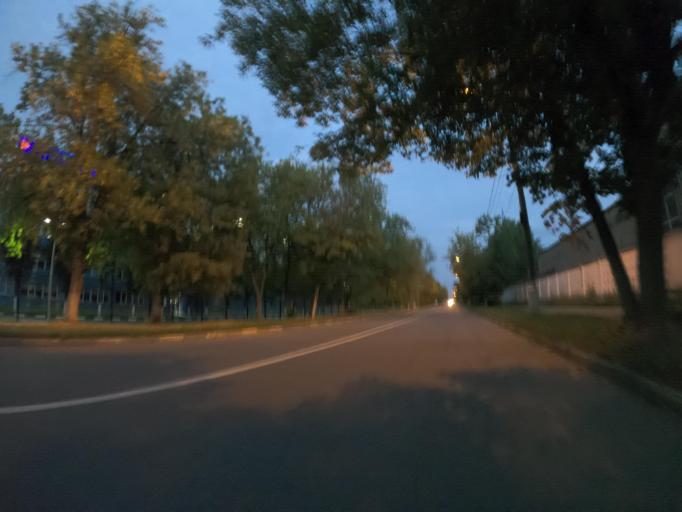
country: RU
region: Moskovskaya
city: Zhukovskiy
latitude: 55.6046
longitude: 38.1183
